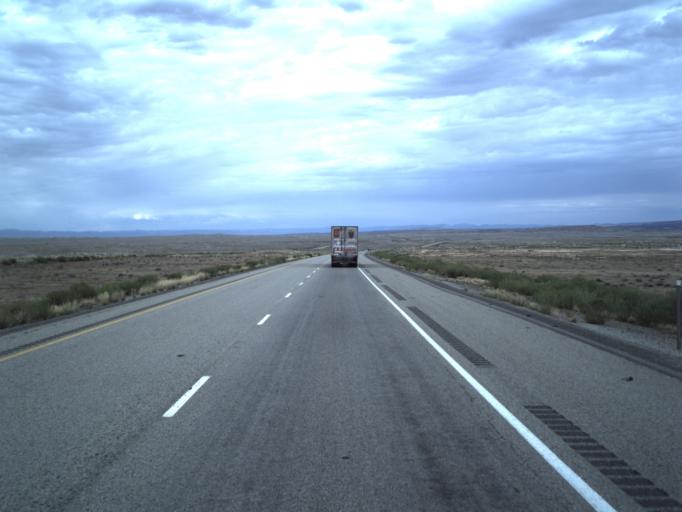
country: US
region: Utah
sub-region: Grand County
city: Moab
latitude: 38.9563
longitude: -109.3850
